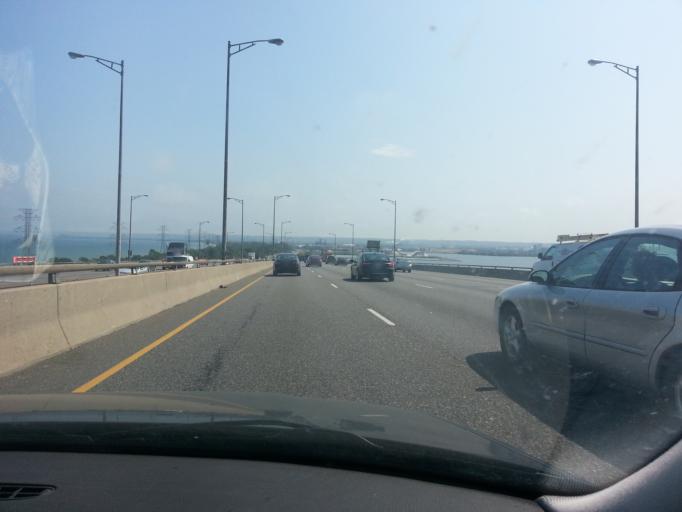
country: CA
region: Ontario
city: Hamilton
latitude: 43.2956
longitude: -79.7959
